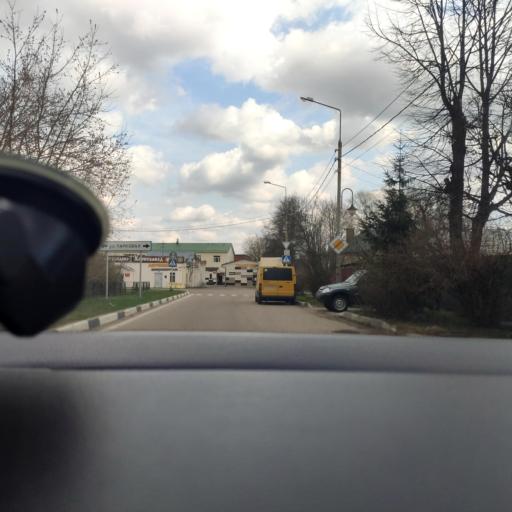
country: RU
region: Moskovskaya
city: Zvenigorod
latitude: 55.7345
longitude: 36.8666
